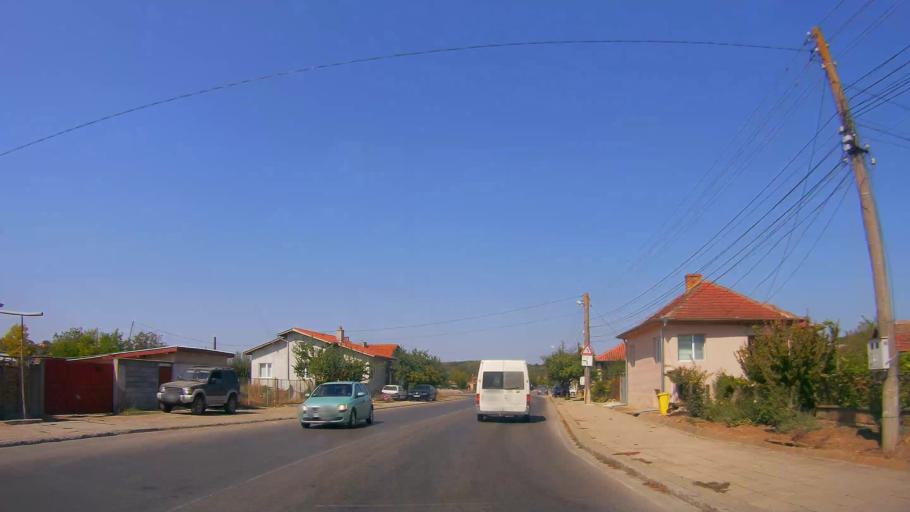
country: BG
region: Razgrad
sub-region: Obshtina Tsar Kaloyan
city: Tsar Kaloyan
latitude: 43.6018
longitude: 26.2447
